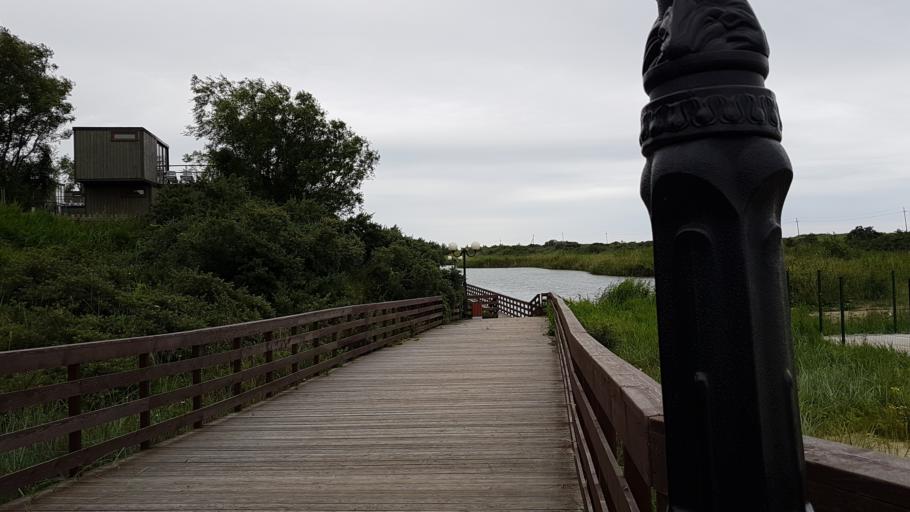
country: RU
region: Kaliningrad
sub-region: Gorod Kaliningrad
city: Yantarnyy
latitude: 54.8829
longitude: 19.9342
